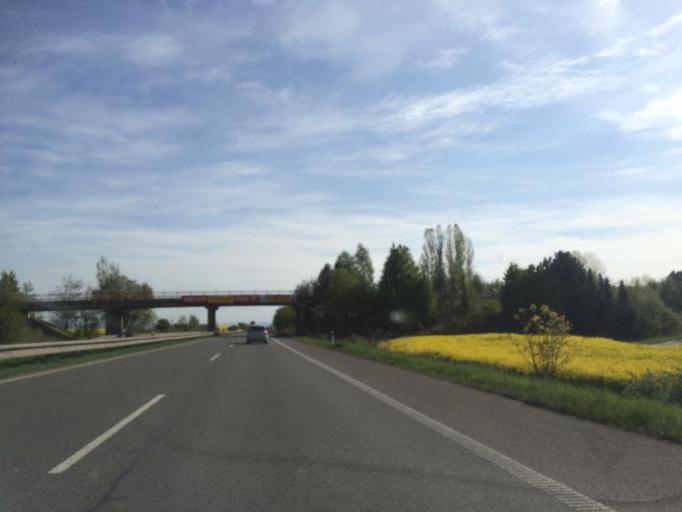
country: CZ
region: Central Bohemia
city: Mnichovo Hradiste
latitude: 50.5267
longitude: 15.0029
